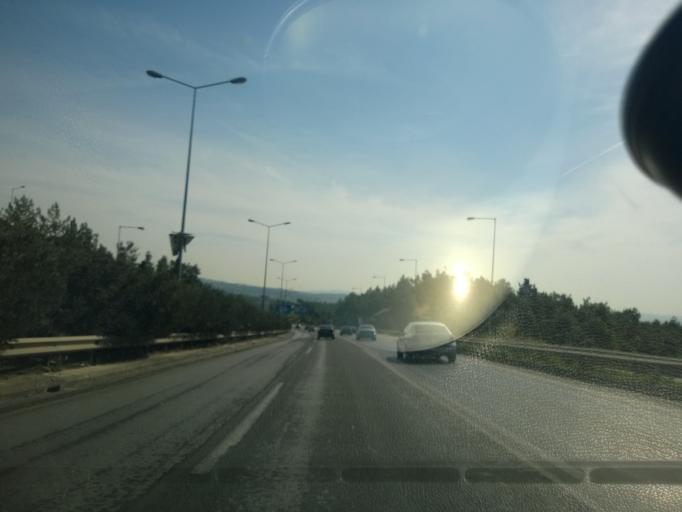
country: GR
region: Central Macedonia
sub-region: Nomos Thessalonikis
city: Agios Pavlos
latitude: 40.6321
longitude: 22.9738
